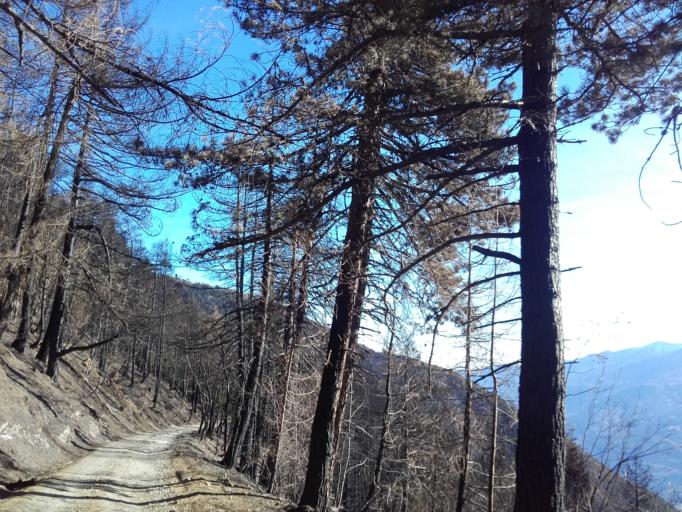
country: IT
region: Piedmont
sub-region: Provincia di Torino
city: Mompantero
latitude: 45.1668
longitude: 7.0392
